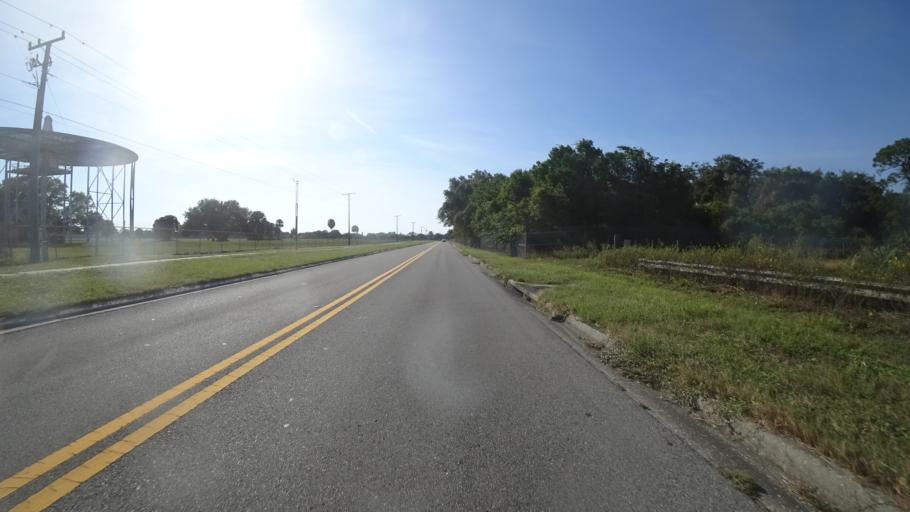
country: US
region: Florida
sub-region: Manatee County
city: Whitfield
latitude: 27.4076
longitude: -82.5631
